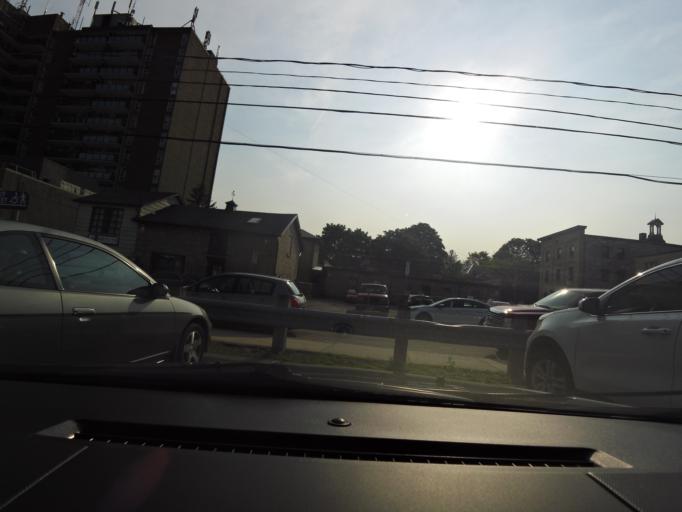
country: CA
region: Ontario
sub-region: Wellington County
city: Guelph
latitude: 43.5463
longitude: -80.2515
